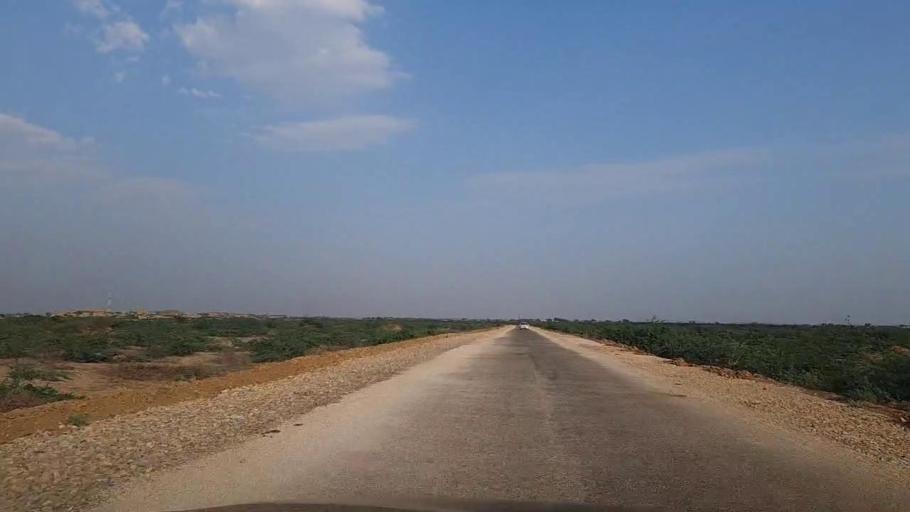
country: PK
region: Sindh
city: Thatta
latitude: 24.8462
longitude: 67.7553
